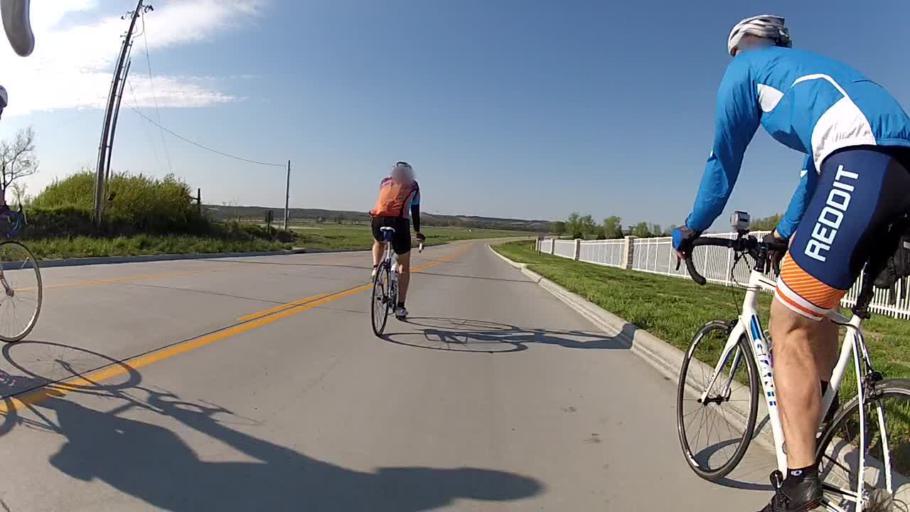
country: US
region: Kansas
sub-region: Riley County
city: Ogden
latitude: 39.1351
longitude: -96.6820
